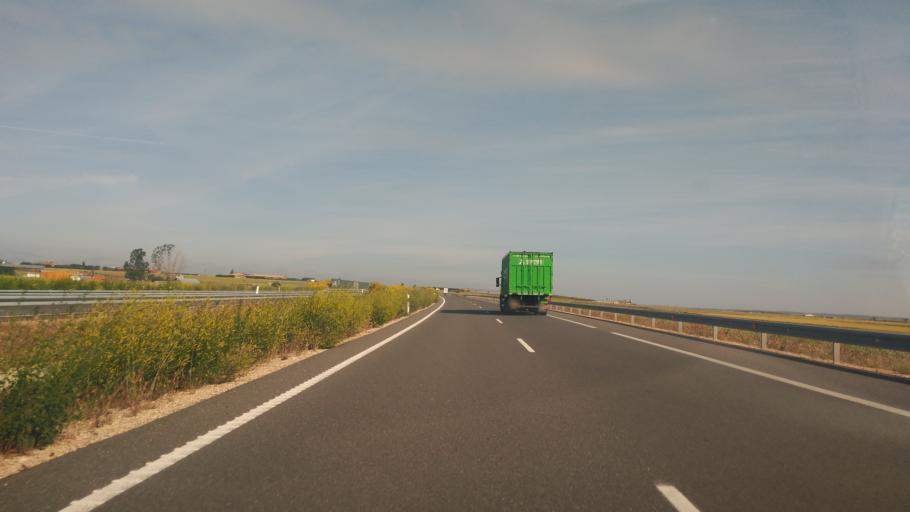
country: ES
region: Castille and Leon
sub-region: Provincia de Salamanca
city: Castellanos de Villiquera
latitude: 41.0530
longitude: -5.6725
